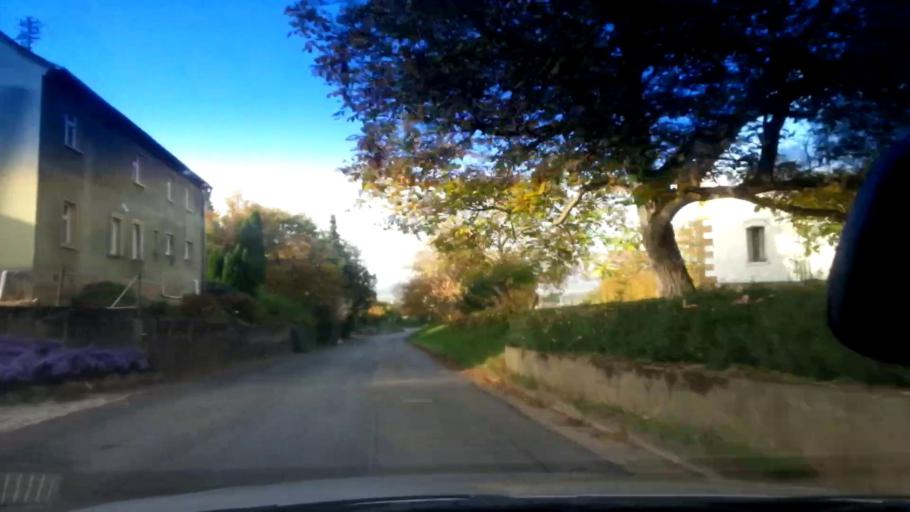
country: DE
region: Bavaria
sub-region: Upper Franconia
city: Schesslitz
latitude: 49.9619
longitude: 11.0564
